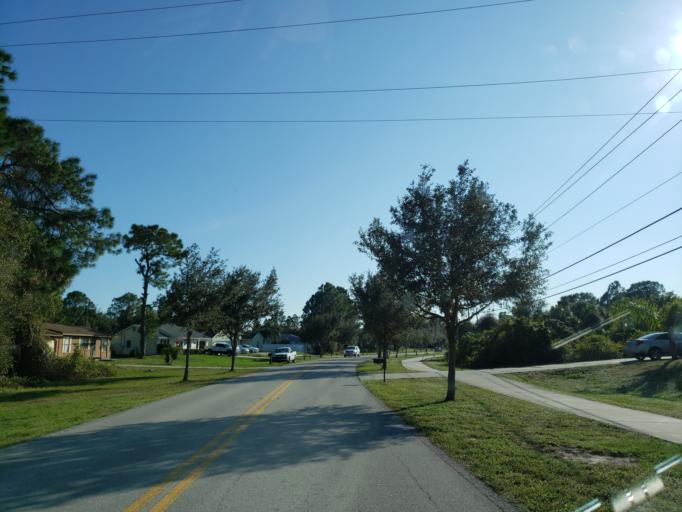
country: US
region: Florida
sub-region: Sarasota County
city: North Port
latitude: 27.0758
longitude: -82.1953
